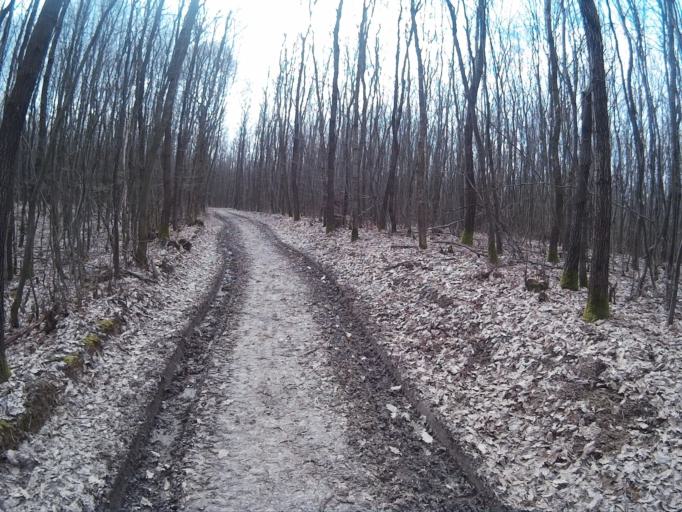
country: HU
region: Pest
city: Kosd
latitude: 47.8452
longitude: 19.1875
